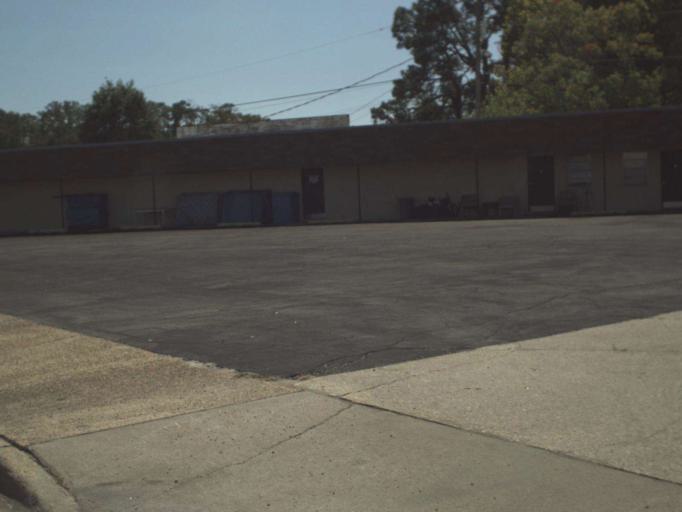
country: US
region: Florida
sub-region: Bay County
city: Springfield
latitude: 30.1553
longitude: -85.6198
